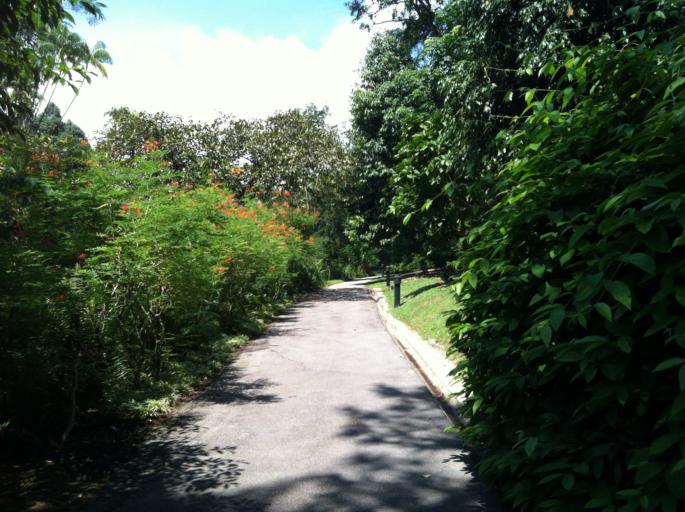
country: SG
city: Singapore
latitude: 1.3082
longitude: 103.8155
